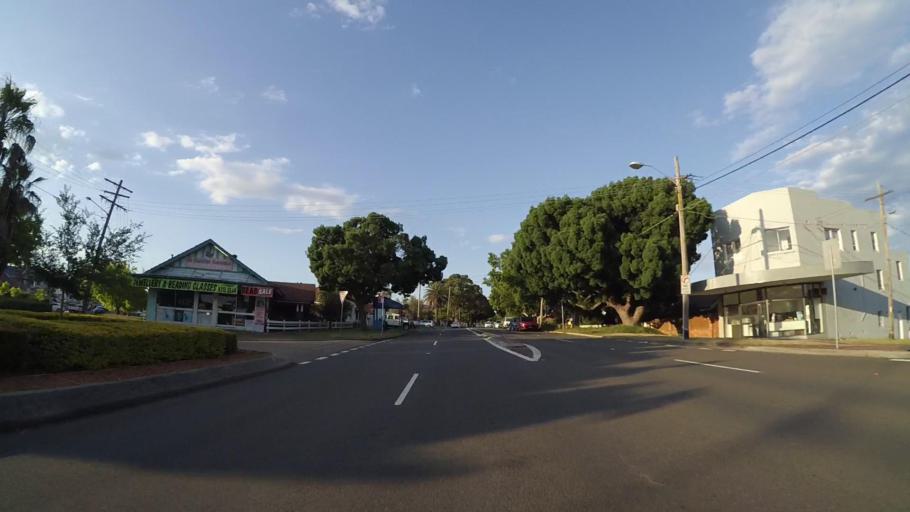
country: AU
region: New South Wales
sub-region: Randwick
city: Daceyville
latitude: -33.9373
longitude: 151.2296
